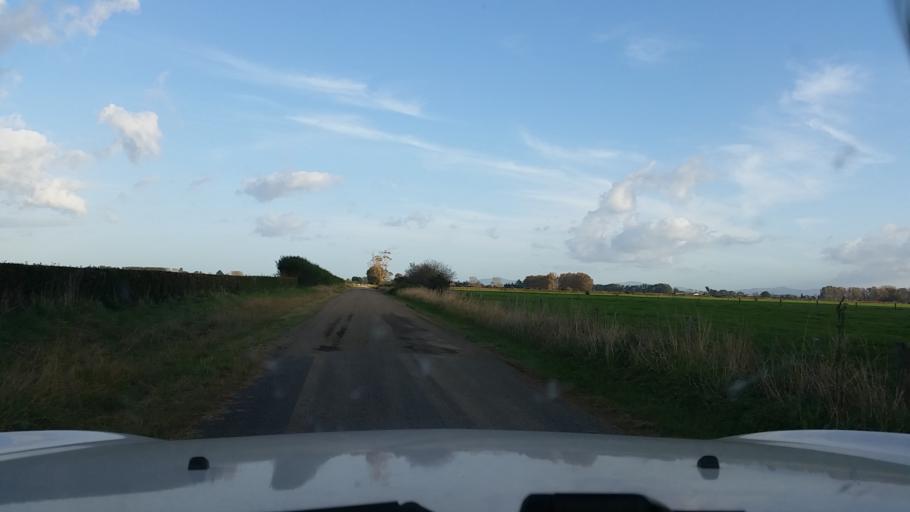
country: NZ
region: Bay of Plenty
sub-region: Western Bay of Plenty District
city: Katikati
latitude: -37.5820
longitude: 175.7131
